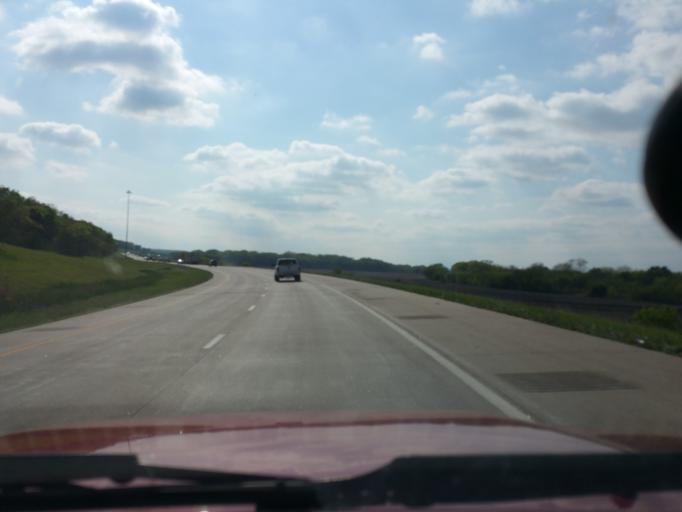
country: US
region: Kansas
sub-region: Pottawatomie County
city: Saint Marys
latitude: 39.0610
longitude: -96.1209
